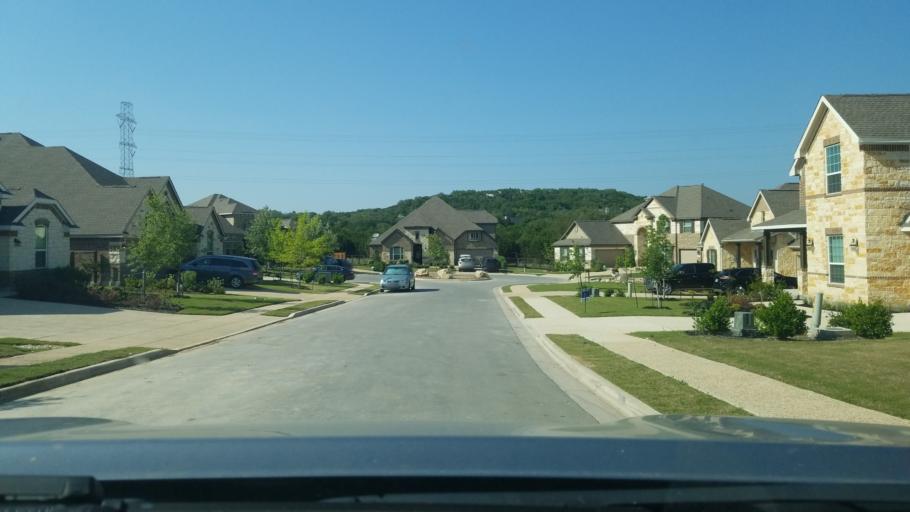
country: US
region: Texas
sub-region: Comal County
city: Bulverde
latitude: 29.7760
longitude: -98.4219
